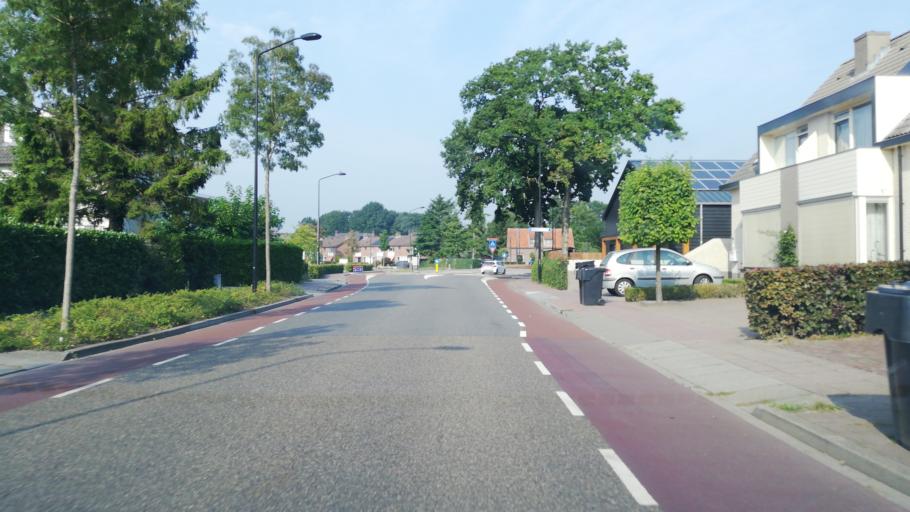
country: NL
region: Gelderland
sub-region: Gemeente Ermelo
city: Ermelo
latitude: 52.2956
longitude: 5.6184
